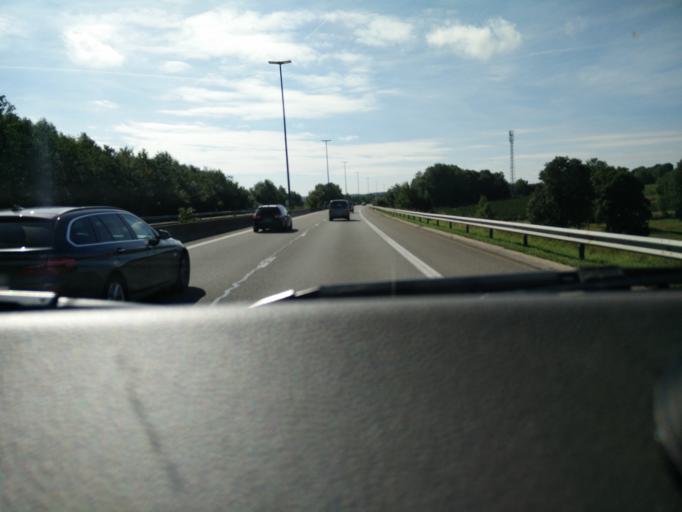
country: BE
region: Wallonia
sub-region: Province du Luxembourg
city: Libin
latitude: 49.9784
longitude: 5.2386
